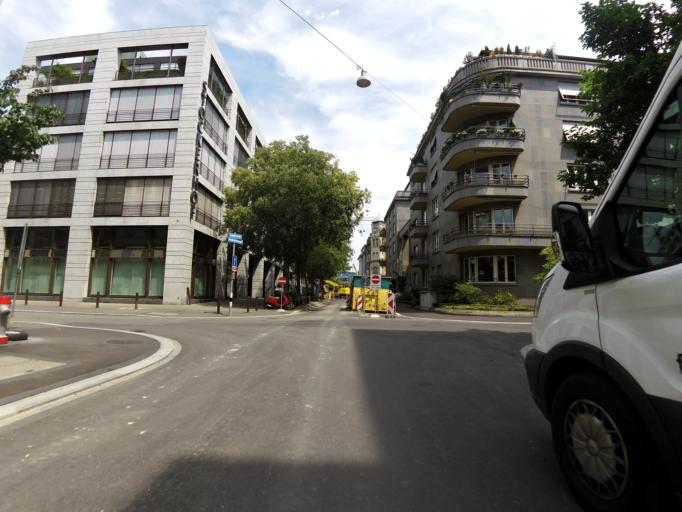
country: CH
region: Zurich
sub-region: Bezirk Zuerich
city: Zuerich (Kreis 2) / Enge
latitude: 47.3655
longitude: 8.5352
